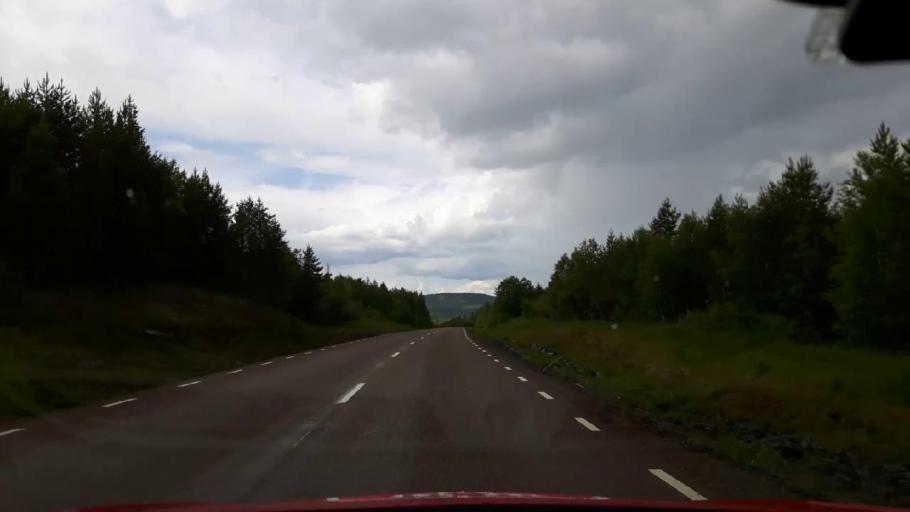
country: SE
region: Jaemtland
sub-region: Krokoms Kommun
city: Valla
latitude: 63.8921
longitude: 14.2655
